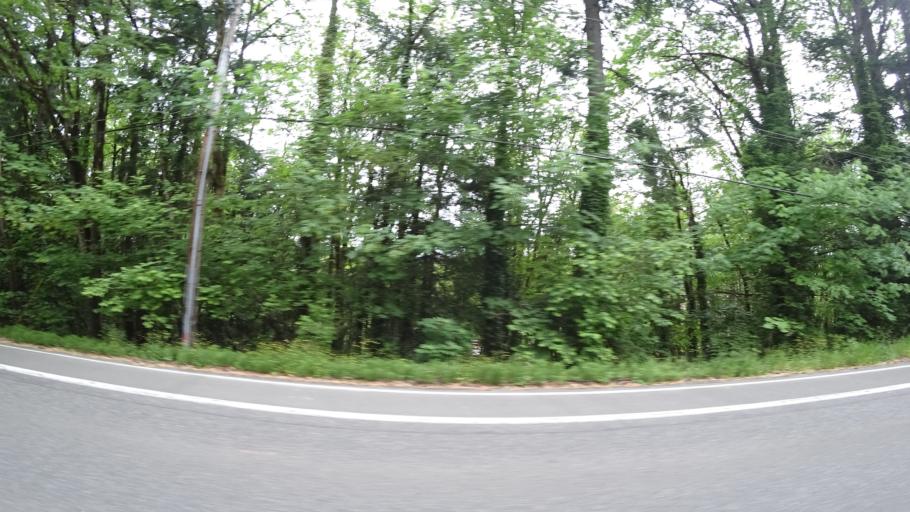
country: US
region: Oregon
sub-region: Washington County
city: Garden Home-Whitford
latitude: 45.4675
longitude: -122.7382
